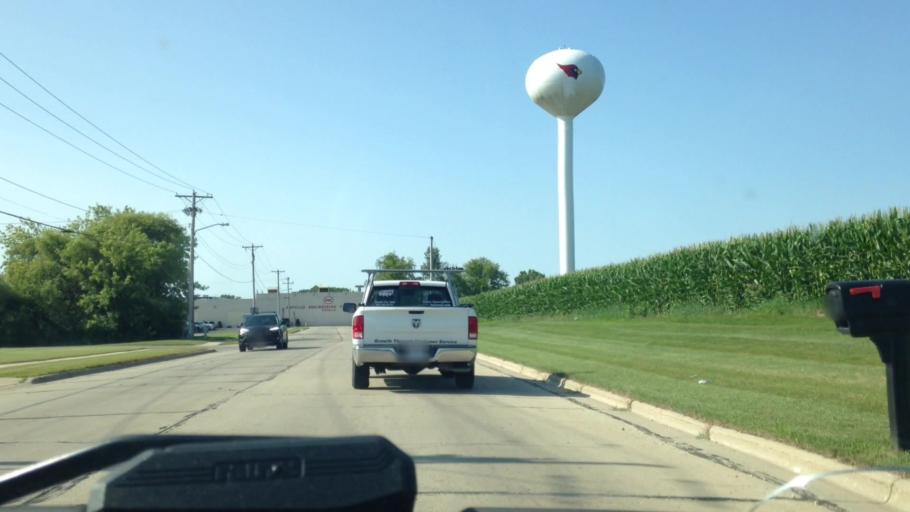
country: US
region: Wisconsin
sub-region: Dodge County
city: Mayville
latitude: 43.4888
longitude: -88.5563
